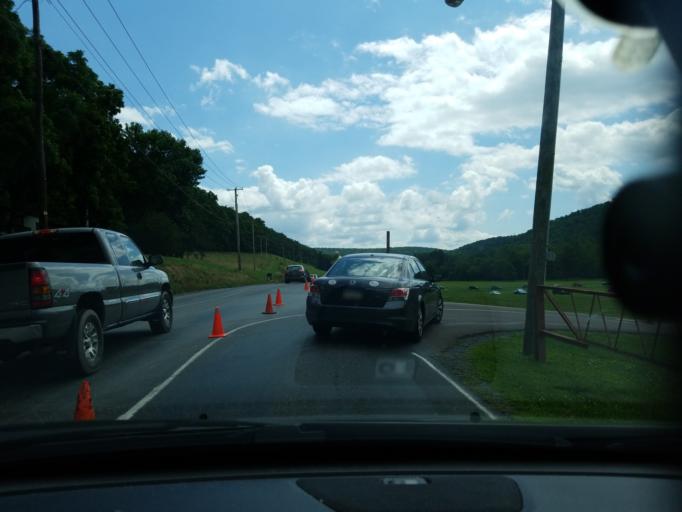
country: US
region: Pennsylvania
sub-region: Northumberland County
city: Elysburg
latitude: 40.8801
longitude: -76.4978
